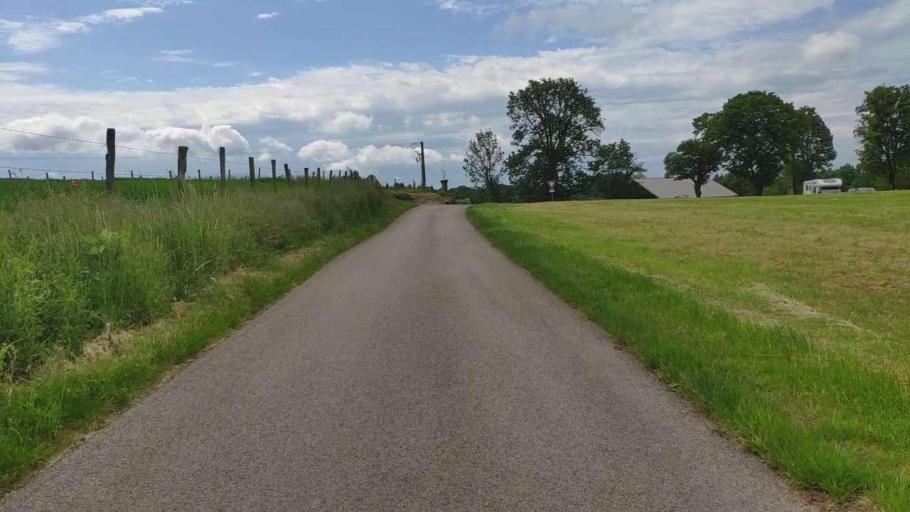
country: FR
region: Franche-Comte
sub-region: Departement du Jura
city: Perrigny
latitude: 46.7557
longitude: 5.6314
